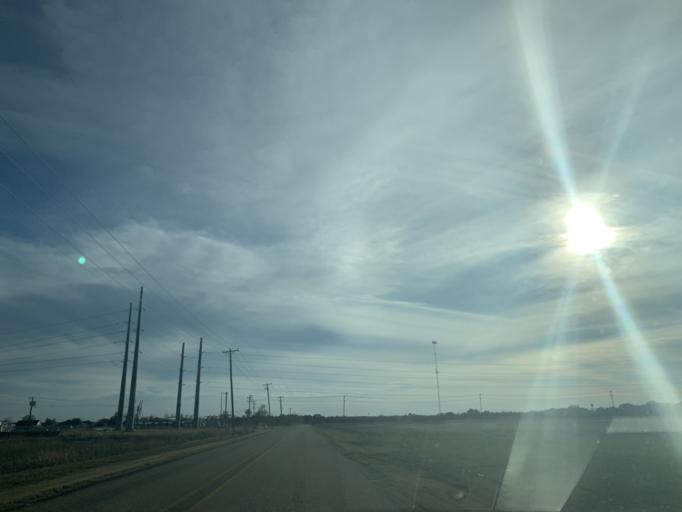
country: US
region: Texas
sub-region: Bell County
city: Salado
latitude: 30.9741
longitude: -97.5126
